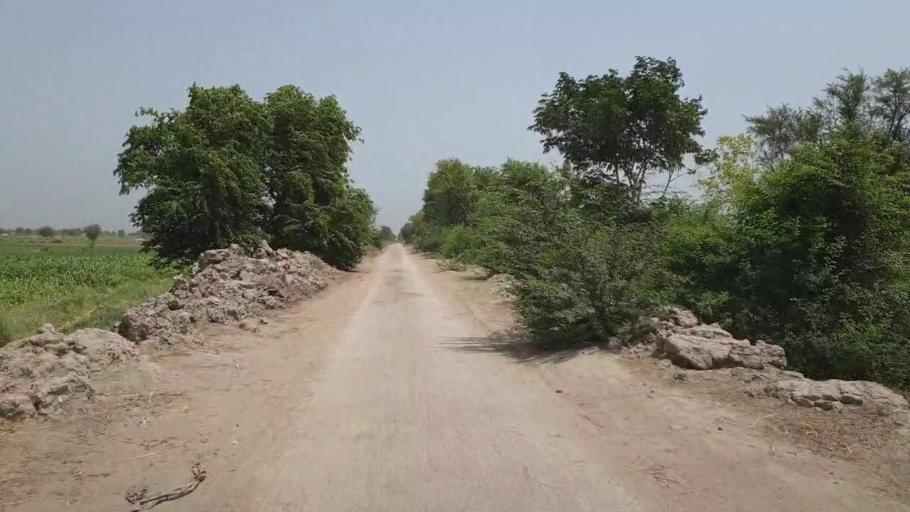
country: PK
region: Sindh
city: Nawabshah
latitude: 26.3069
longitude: 68.3028
